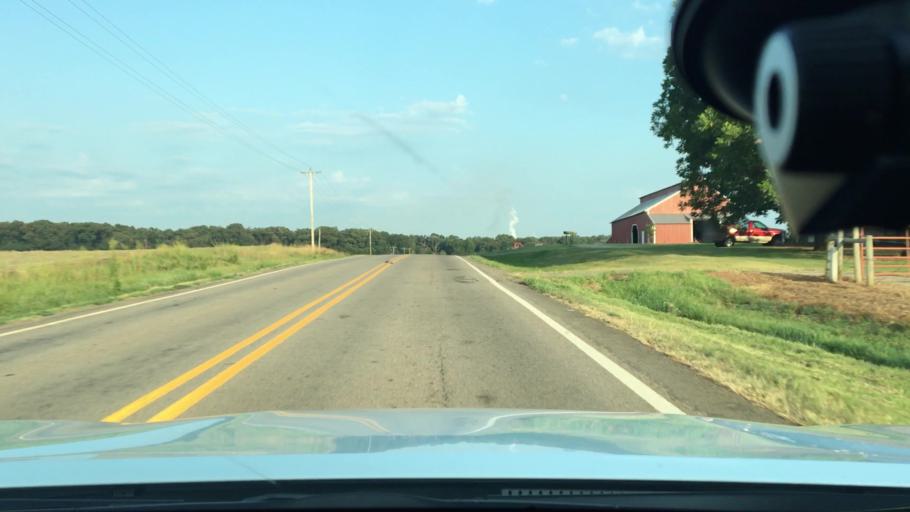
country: US
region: Arkansas
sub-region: Johnson County
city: Clarksville
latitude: 35.3793
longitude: -93.5548
